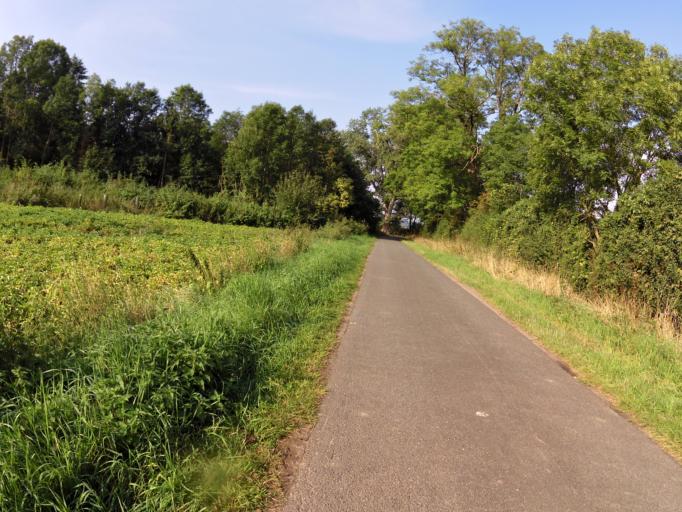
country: DE
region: Lower Saxony
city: Langwedel
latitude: 52.9587
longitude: 9.1837
